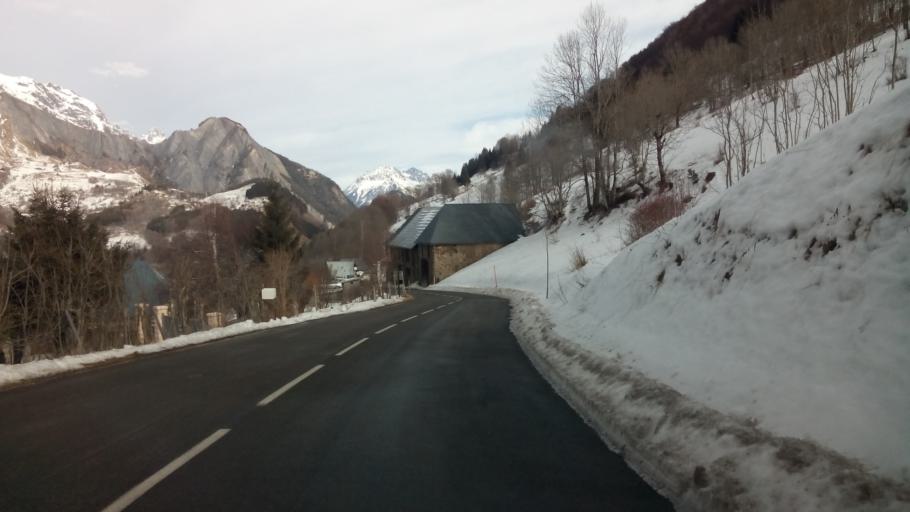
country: FR
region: Rhone-Alpes
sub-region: Departement de l'Isere
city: Livet-et-Gavet
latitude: 45.0287
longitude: 5.9734
